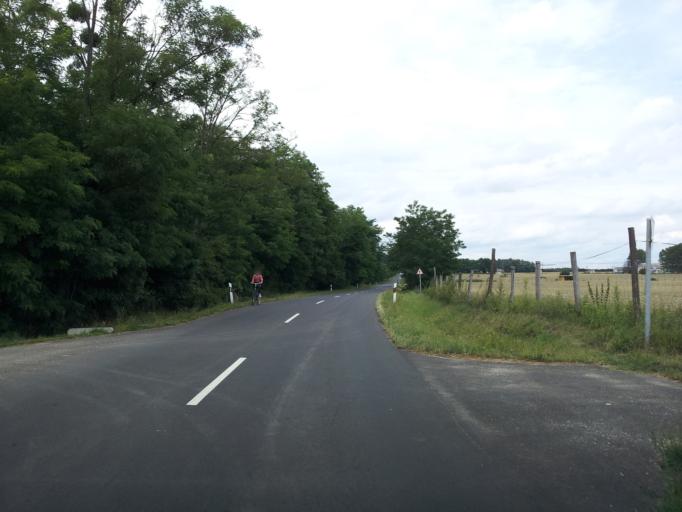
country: HU
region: Zala
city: Zalaszentgrot
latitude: 47.0400
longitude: 16.9880
